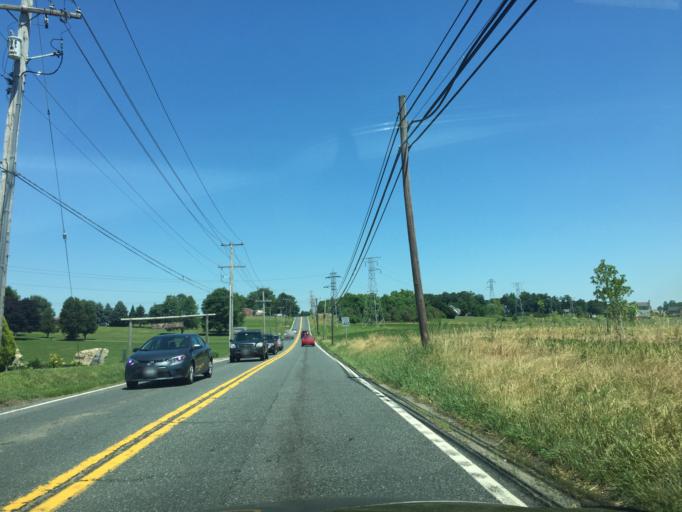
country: US
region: Maryland
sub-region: Harford County
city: Jarrettsville
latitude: 39.5876
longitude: -76.4729
